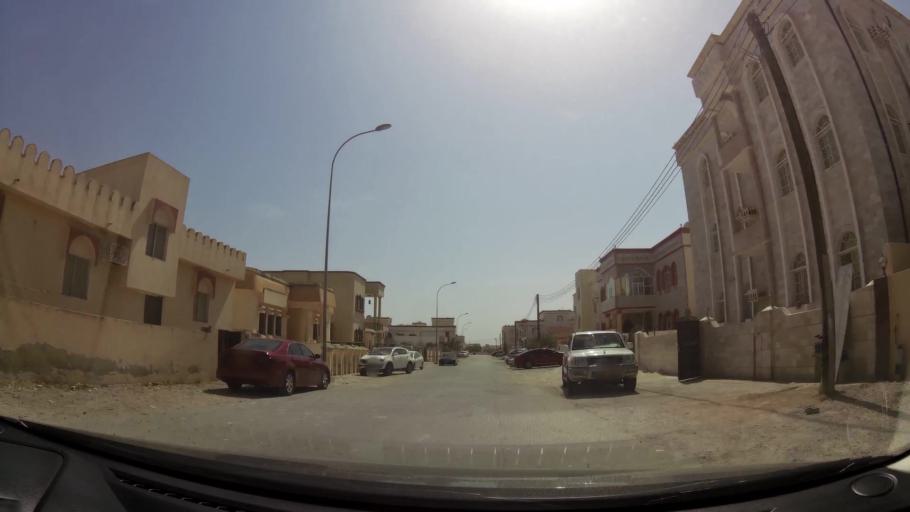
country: OM
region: Zufar
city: Salalah
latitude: 17.0454
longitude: 54.1598
